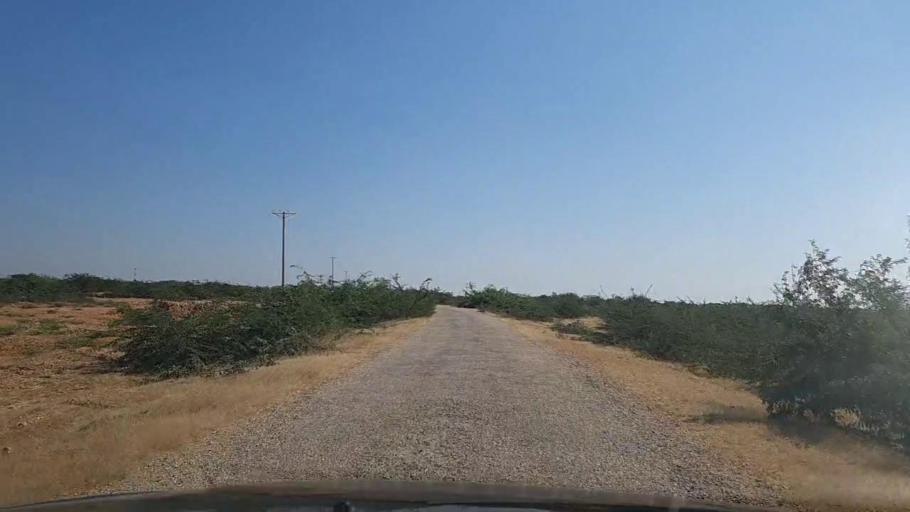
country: PK
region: Sindh
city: Thatta
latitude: 24.6294
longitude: 67.8388
